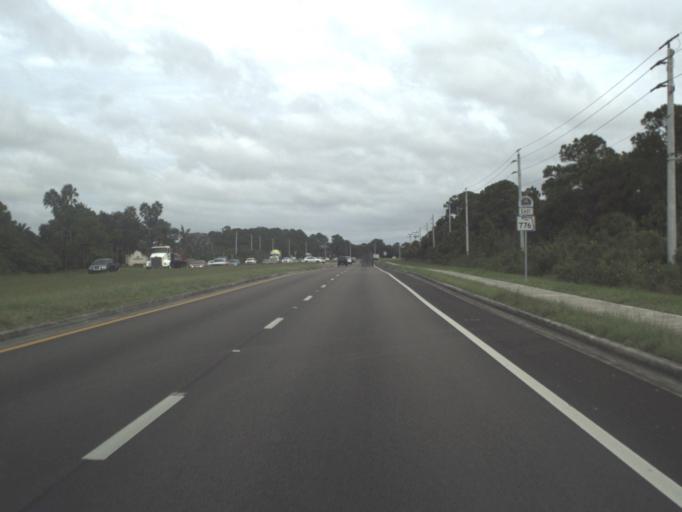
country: US
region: Florida
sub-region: Sarasota County
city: North Port
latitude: 26.9857
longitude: -82.2060
